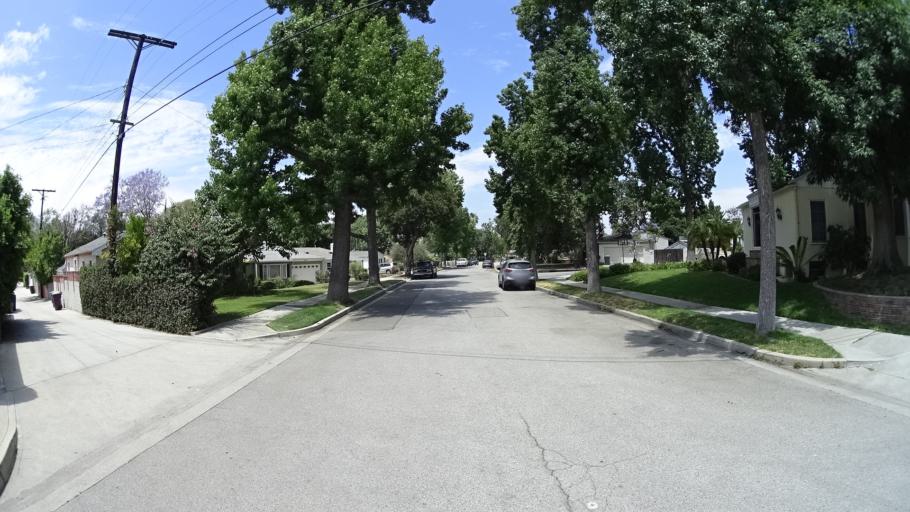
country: US
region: California
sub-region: Los Angeles County
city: Burbank
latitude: 34.1601
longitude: -118.3020
